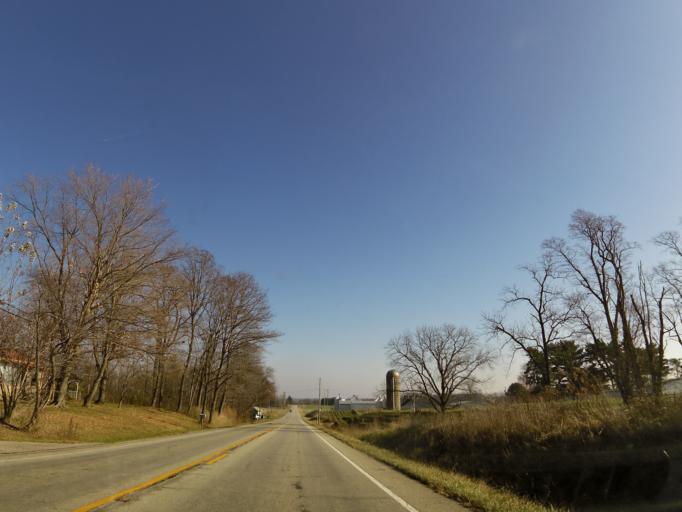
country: US
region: Indiana
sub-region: Fayette County
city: Connersville
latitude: 39.6303
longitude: -85.2406
